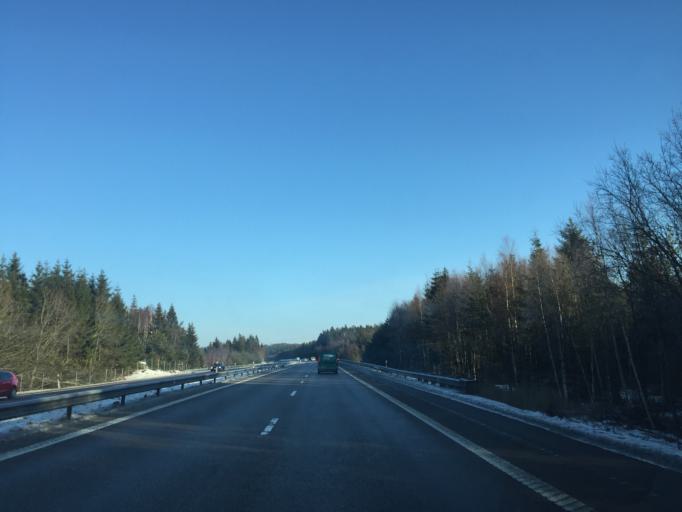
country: SE
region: Vaestra Goetaland
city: Svanesund
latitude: 58.1238
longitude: 11.8827
